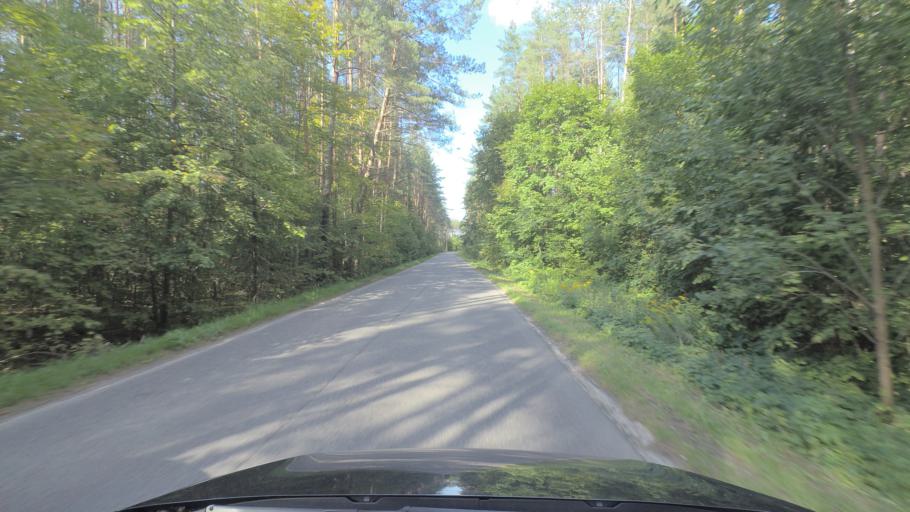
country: LT
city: Nemencine
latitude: 54.8246
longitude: 25.3582
